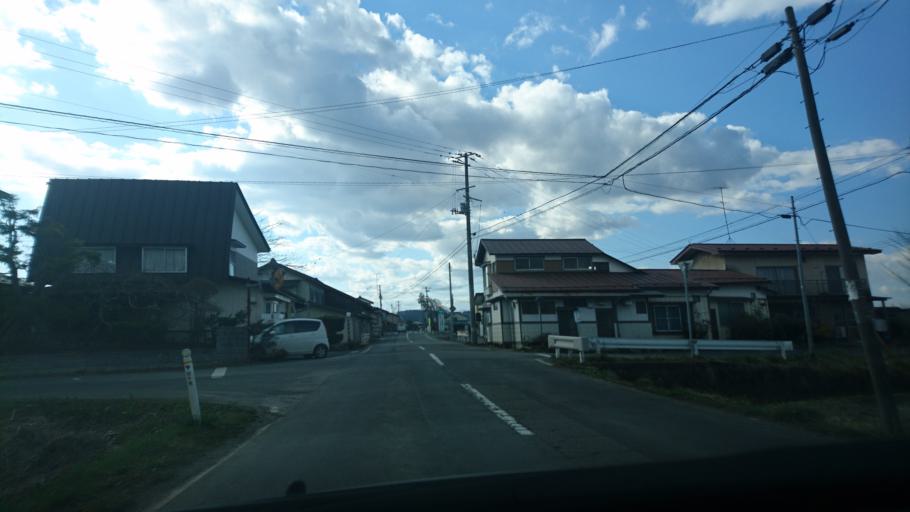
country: JP
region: Iwate
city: Mizusawa
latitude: 39.0424
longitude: 141.1411
